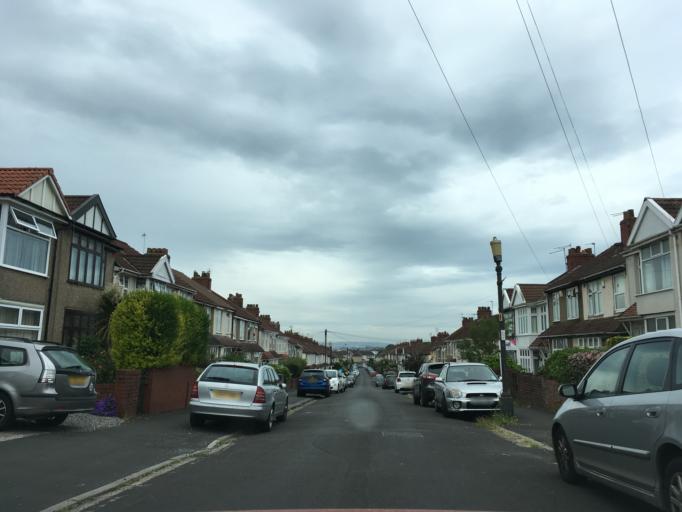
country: GB
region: England
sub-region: South Gloucestershire
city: Stoke Gifford
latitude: 51.4949
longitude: -2.5771
